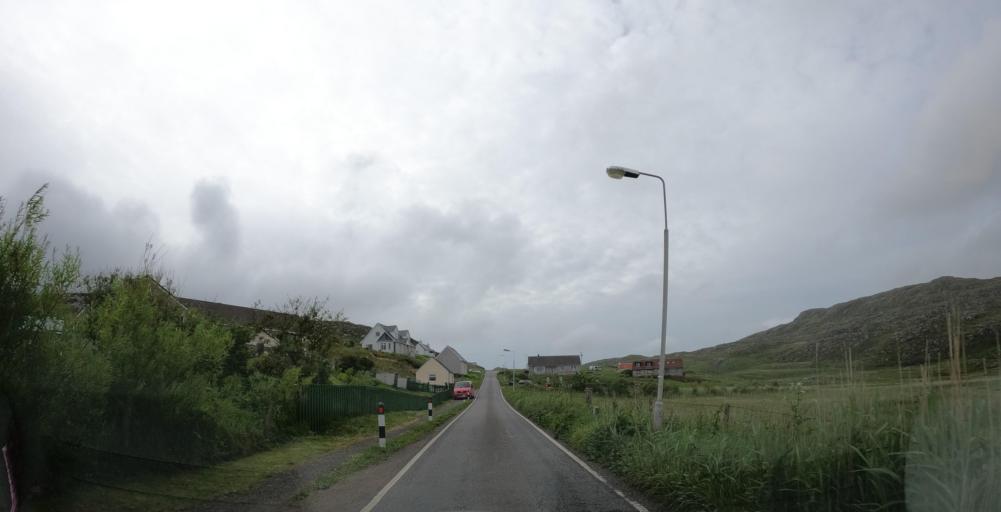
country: GB
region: Scotland
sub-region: Eilean Siar
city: Barra
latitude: 56.9595
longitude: -7.5051
